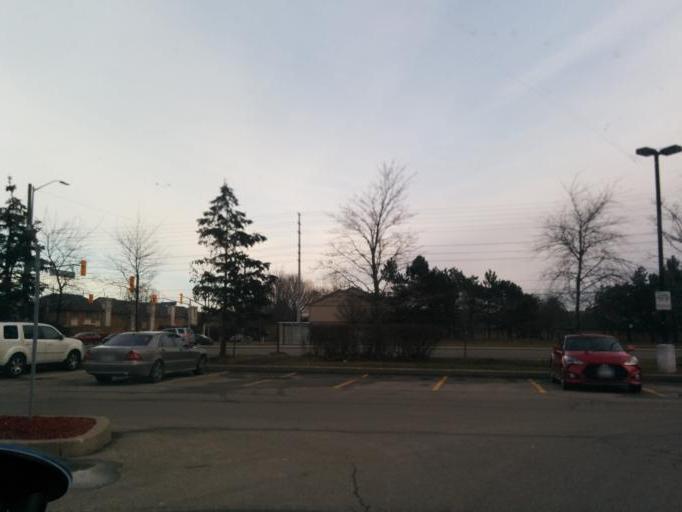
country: CA
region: Ontario
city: Mississauga
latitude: 43.5653
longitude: -79.7003
